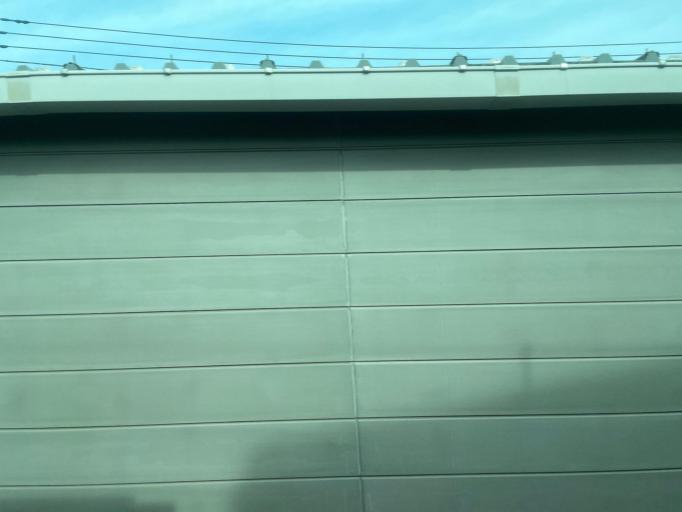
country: JP
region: Tokyo
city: Ome
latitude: 35.7911
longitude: 139.2694
